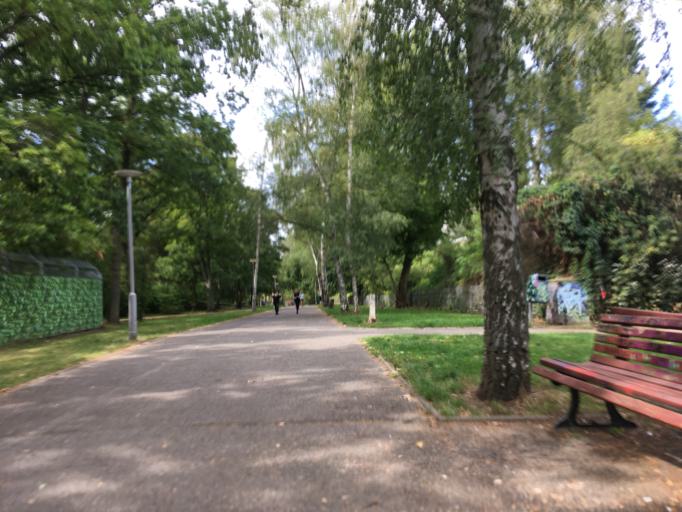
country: DE
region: Berlin
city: Mariendorf
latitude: 52.4445
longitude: 13.3969
